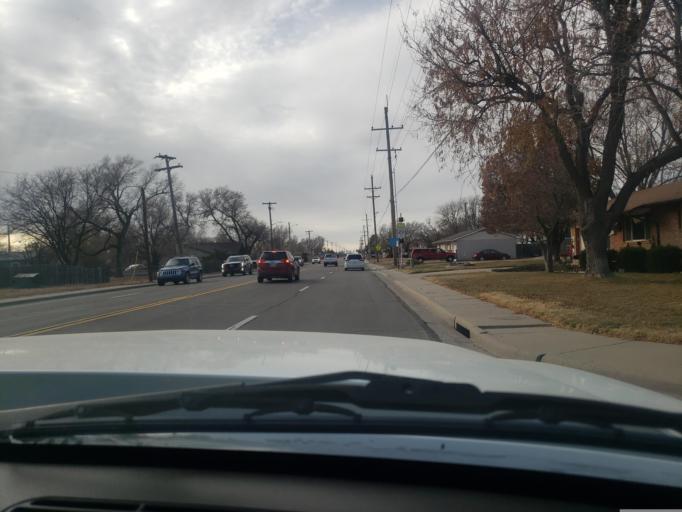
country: US
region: Kansas
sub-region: Finney County
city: Garden City
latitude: 37.9896
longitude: -100.8681
